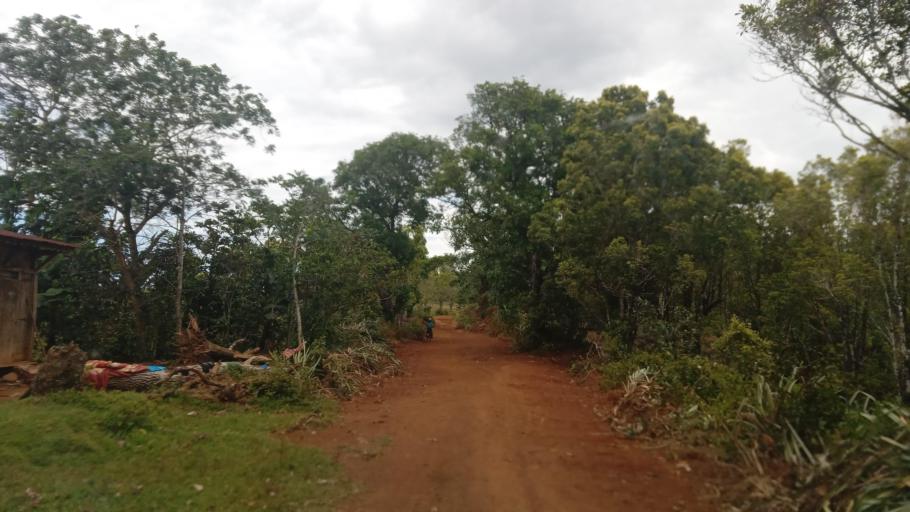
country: MG
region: Atsimo-Atsinanana
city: Vohipaho
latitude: -23.6155
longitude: 47.5822
